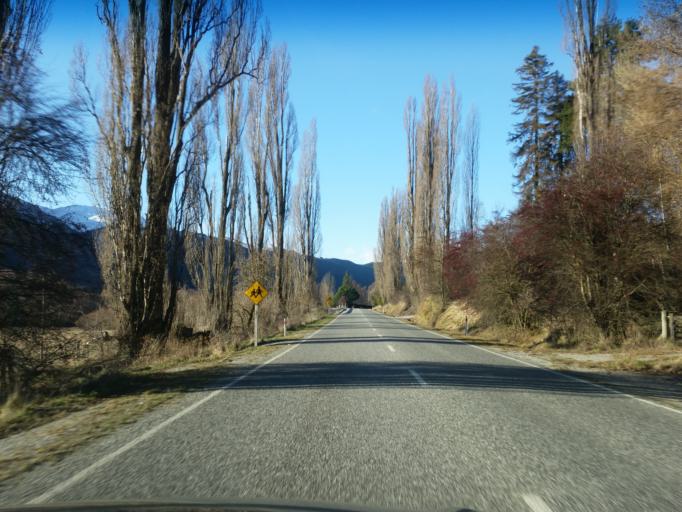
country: NZ
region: Otago
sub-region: Queenstown-Lakes District
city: Arrowtown
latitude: -44.9574
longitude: 168.7322
